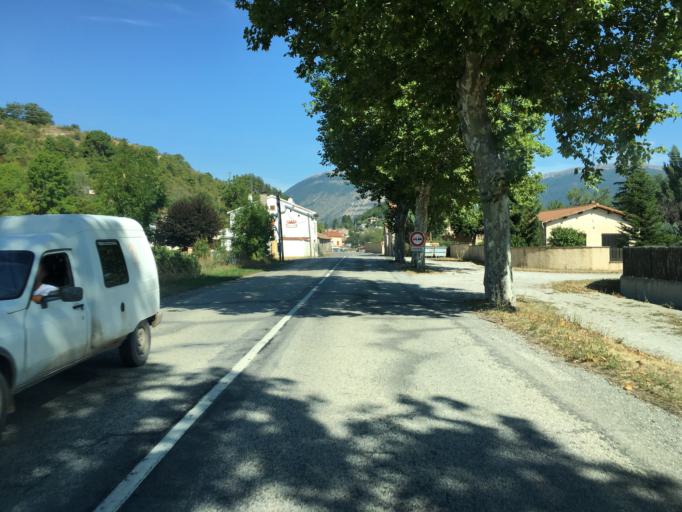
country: FR
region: Provence-Alpes-Cote d'Azur
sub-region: Departement des Hautes-Alpes
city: Serres
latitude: 44.4900
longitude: 5.7288
